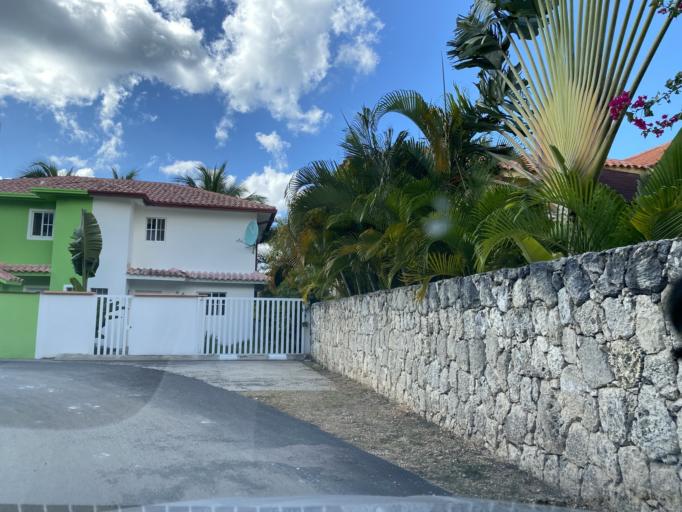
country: DO
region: La Romana
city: La Romana
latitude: 18.3501
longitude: -68.8274
